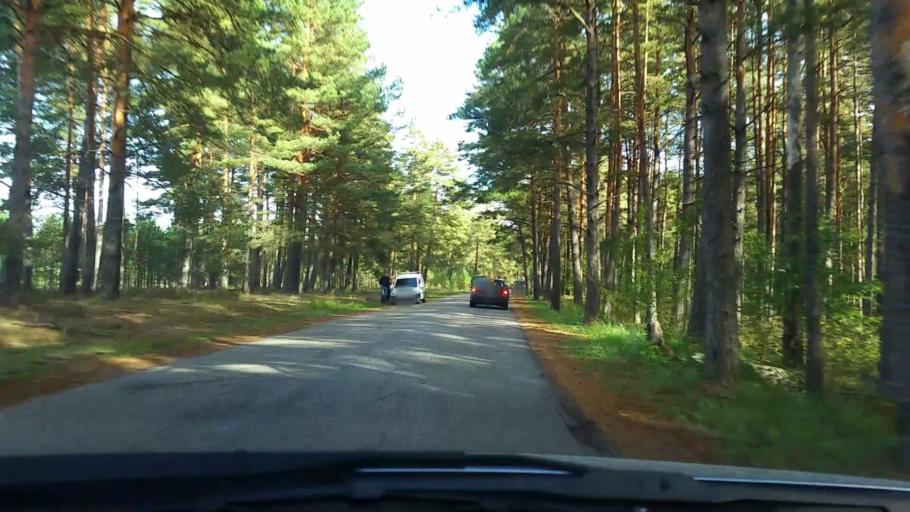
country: LV
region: Adazi
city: Adazi
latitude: 57.1018
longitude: 24.3749
